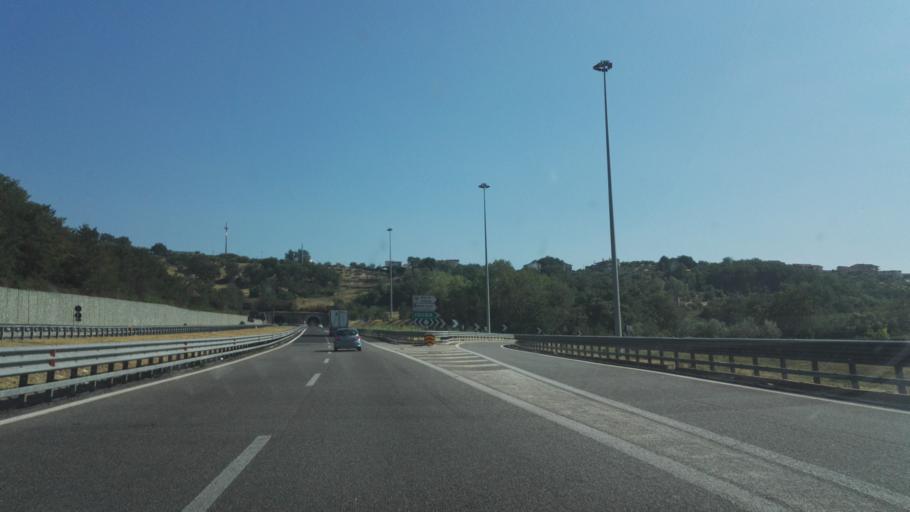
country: IT
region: Calabria
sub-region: Provincia di Cosenza
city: Rosario
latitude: 39.3002
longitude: 16.2359
